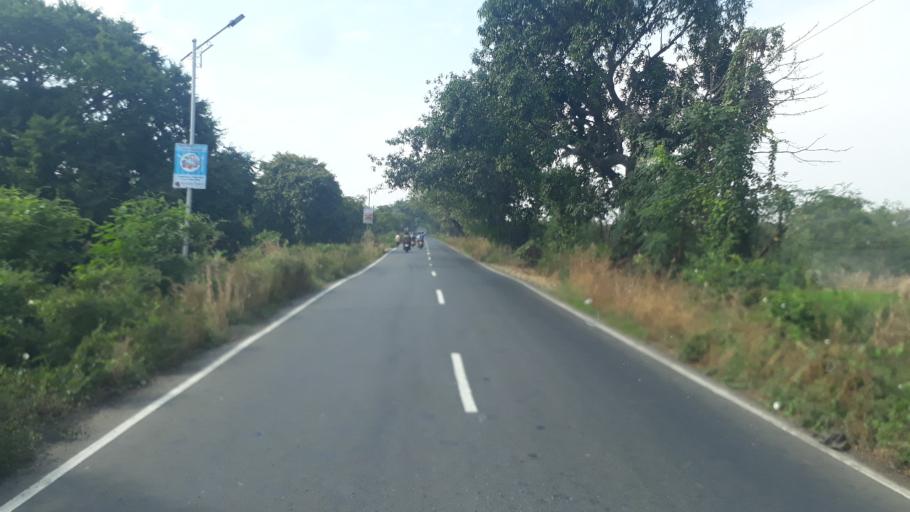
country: IN
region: Maharashtra
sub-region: Raigarh
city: Alibag
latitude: 18.6720
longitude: 72.9097
